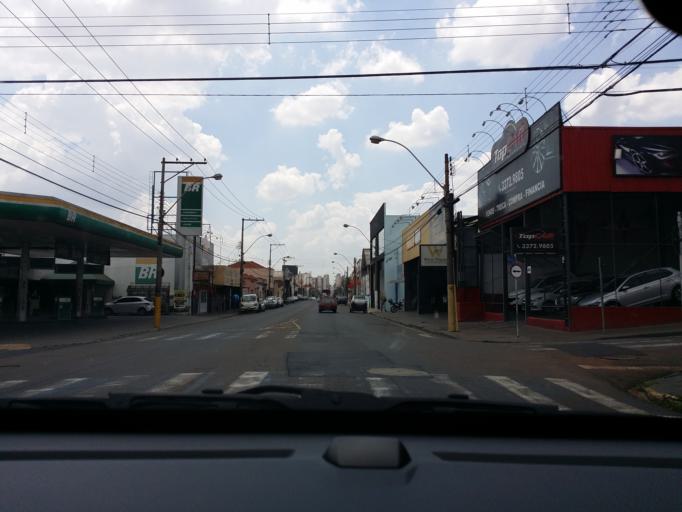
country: BR
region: Sao Paulo
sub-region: Sao Carlos
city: Sao Carlos
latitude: -22.0304
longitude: -47.8903
